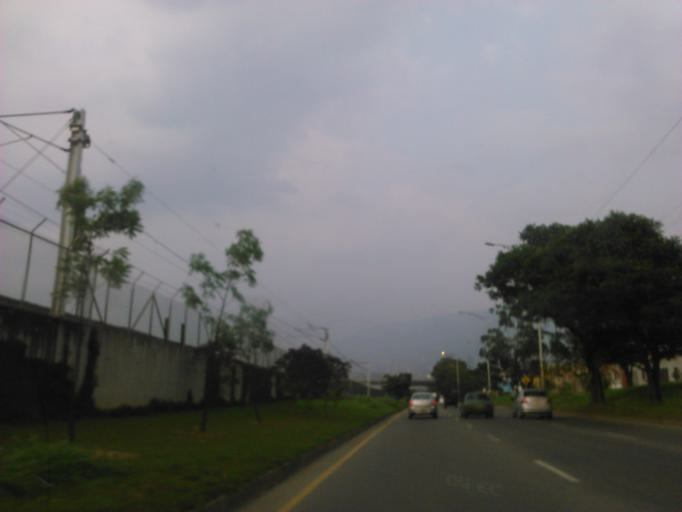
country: CO
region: Antioquia
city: Sabaneta
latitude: 6.1581
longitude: -75.6151
